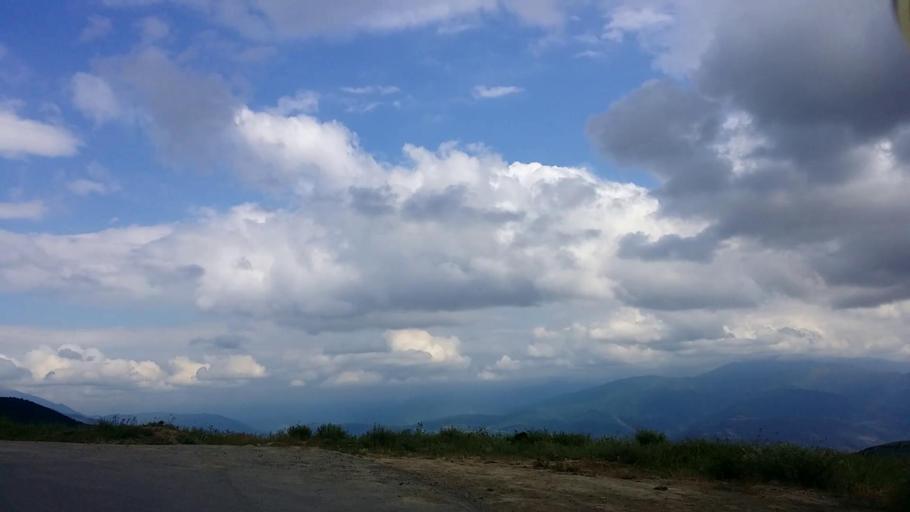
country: IR
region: Mazandaran
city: Chalus
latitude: 36.5518
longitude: 51.2800
